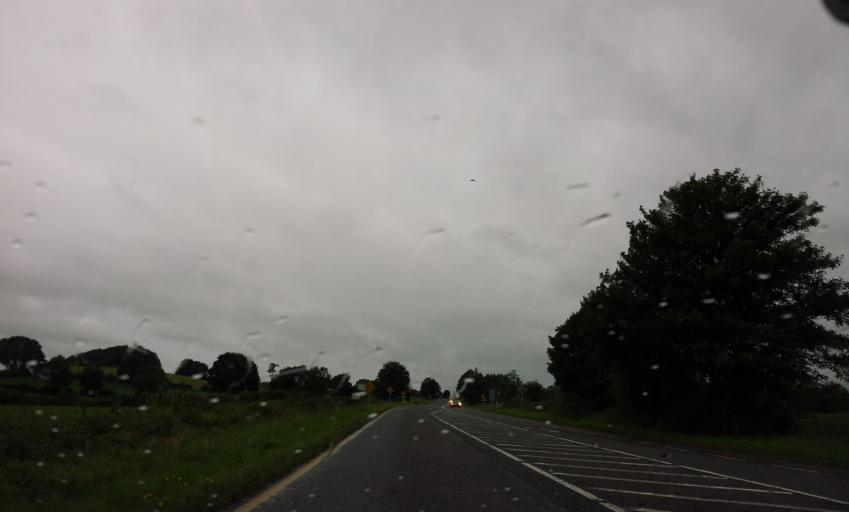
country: IE
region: Munster
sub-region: County Cork
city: Mitchelstown
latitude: 52.2786
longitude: -8.2515
